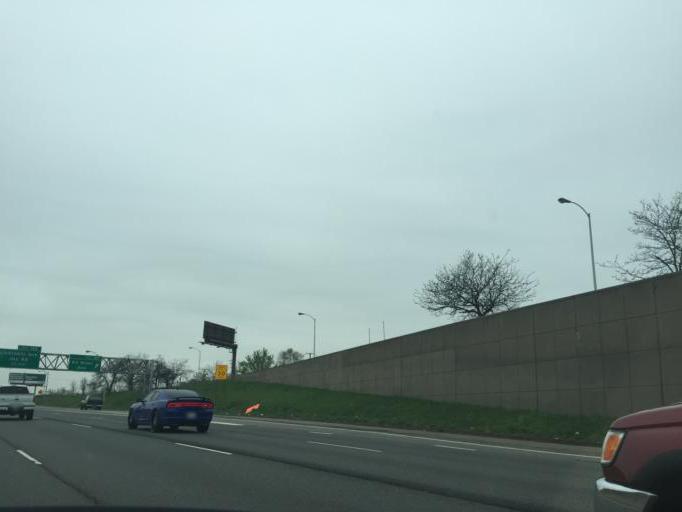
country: US
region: Michigan
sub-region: Wayne County
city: Highland Park
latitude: 42.3757
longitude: -83.1464
